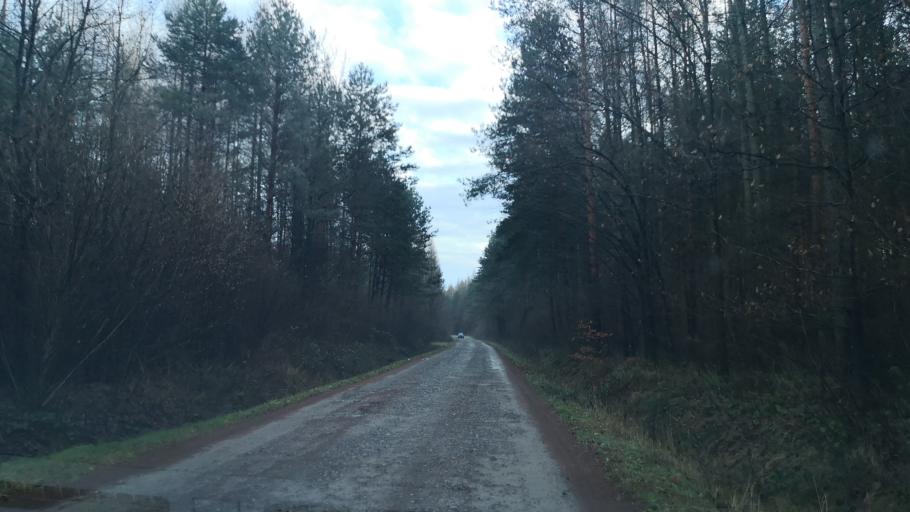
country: PL
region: Subcarpathian Voivodeship
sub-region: Powiat lezajski
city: Piskorowice
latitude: 50.2540
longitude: 22.5629
